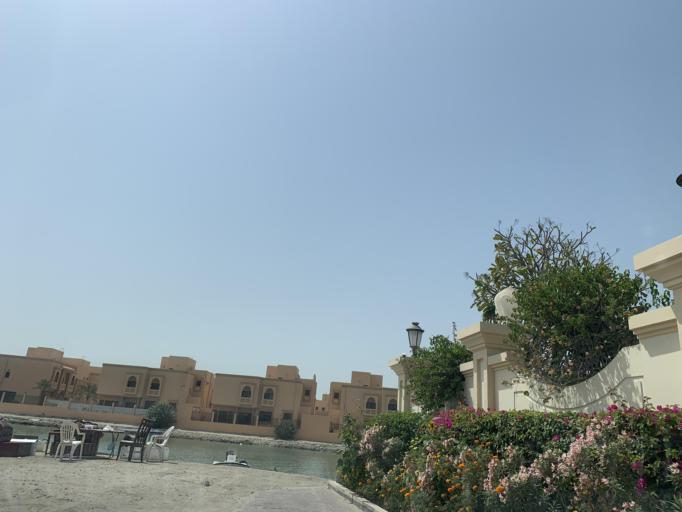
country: BH
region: Manama
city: Manama
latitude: 26.2019
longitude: 50.5714
